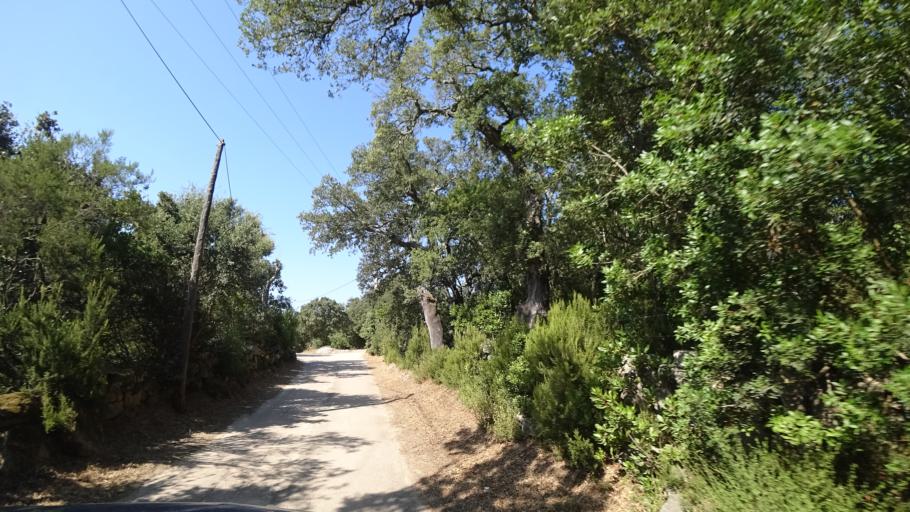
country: FR
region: Corsica
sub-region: Departement de la Corse-du-Sud
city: Porto-Vecchio
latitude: 41.5664
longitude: 9.2123
